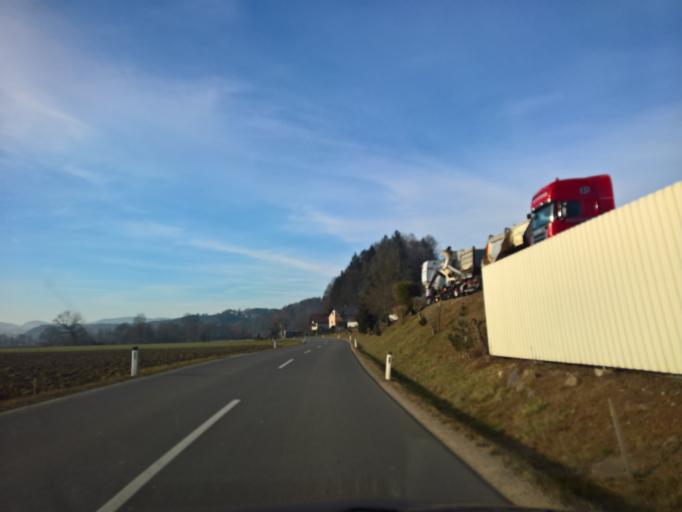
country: AT
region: Styria
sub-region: Politischer Bezirk Leibnitz
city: Sankt Johann im Saggautal
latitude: 46.6980
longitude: 15.3813
